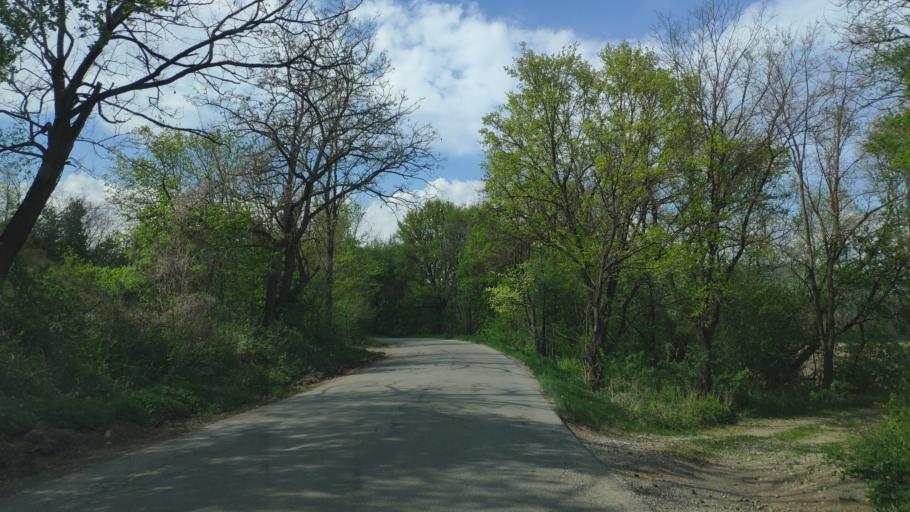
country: SK
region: Kosicky
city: Moldava nad Bodvou
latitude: 48.5883
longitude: 20.9114
